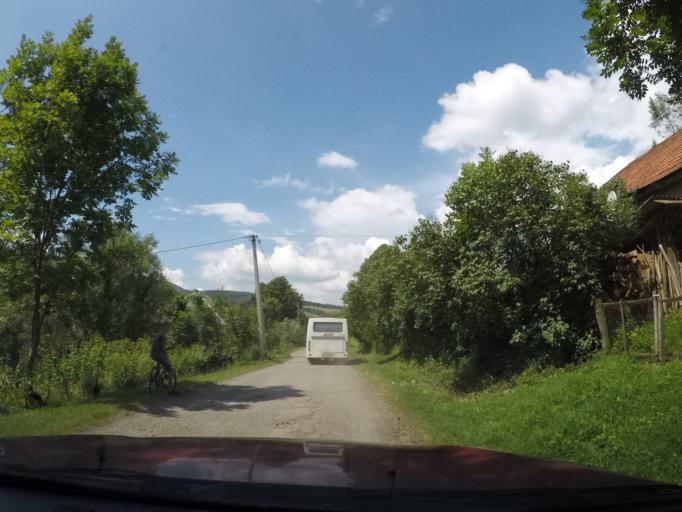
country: UA
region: Zakarpattia
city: Velykyi Bereznyi
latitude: 49.0271
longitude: 22.5995
